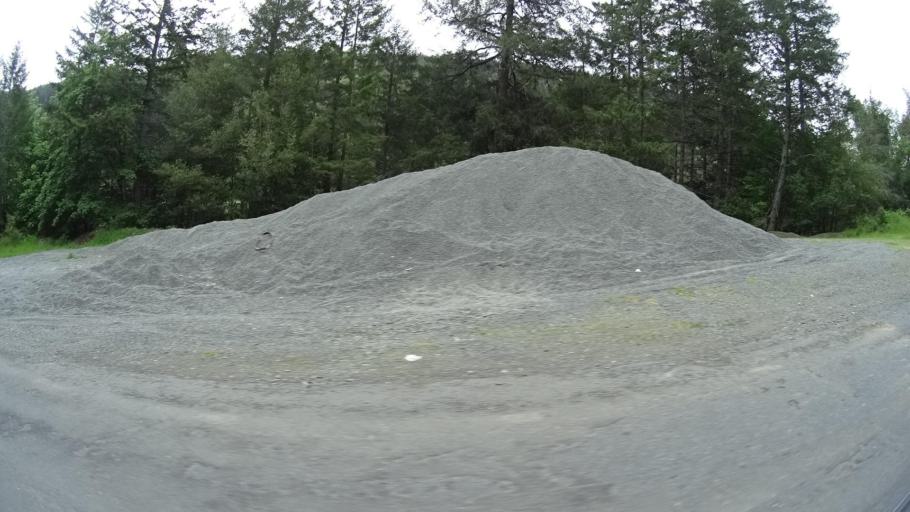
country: US
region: California
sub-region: Humboldt County
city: Willow Creek
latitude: 41.2054
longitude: -123.7566
